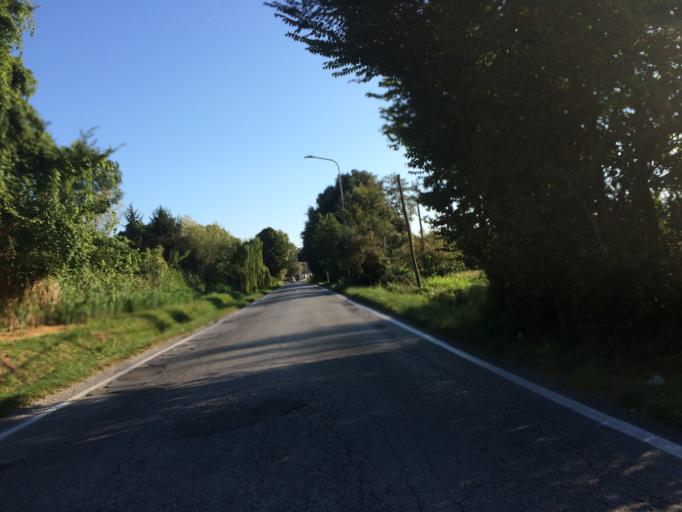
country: IT
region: Tuscany
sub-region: Provincia di Lucca
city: Camaiore
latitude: 43.8918
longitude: 10.2480
